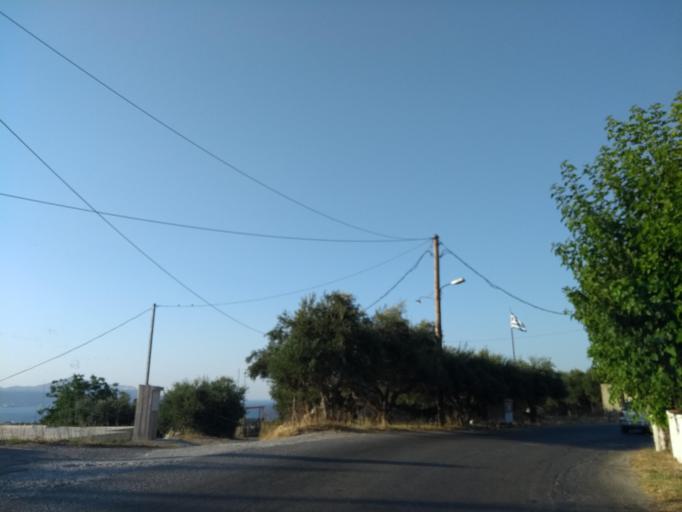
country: GR
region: Crete
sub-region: Nomos Chanias
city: Kalivai
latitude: 35.4364
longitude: 24.1777
